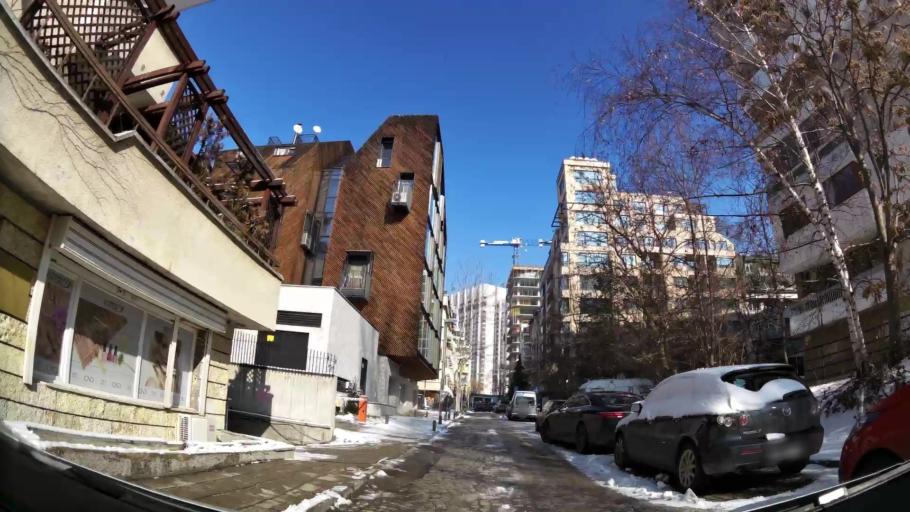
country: BG
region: Sofia-Capital
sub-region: Stolichna Obshtina
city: Sofia
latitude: 42.6699
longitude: 23.3175
